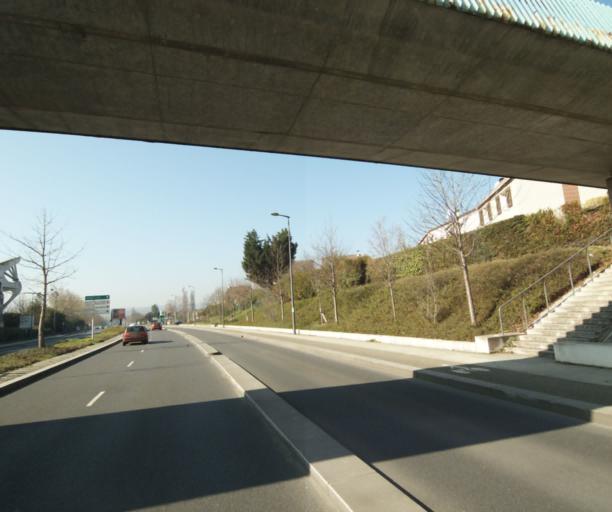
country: FR
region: Ile-de-France
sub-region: Departement du Val-d'Oise
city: Cergy
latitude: 49.0313
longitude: 2.0723
